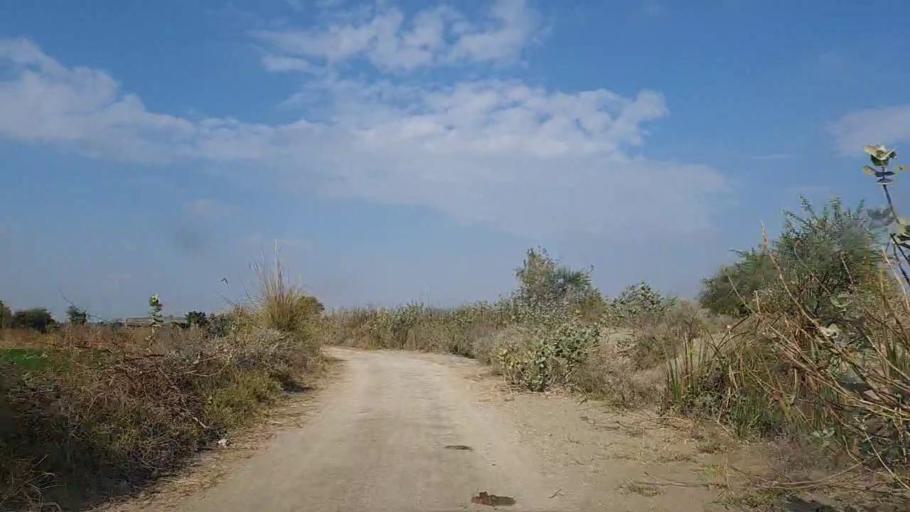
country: PK
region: Sindh
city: Sanghar
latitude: 26.2684
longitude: 69.0120
